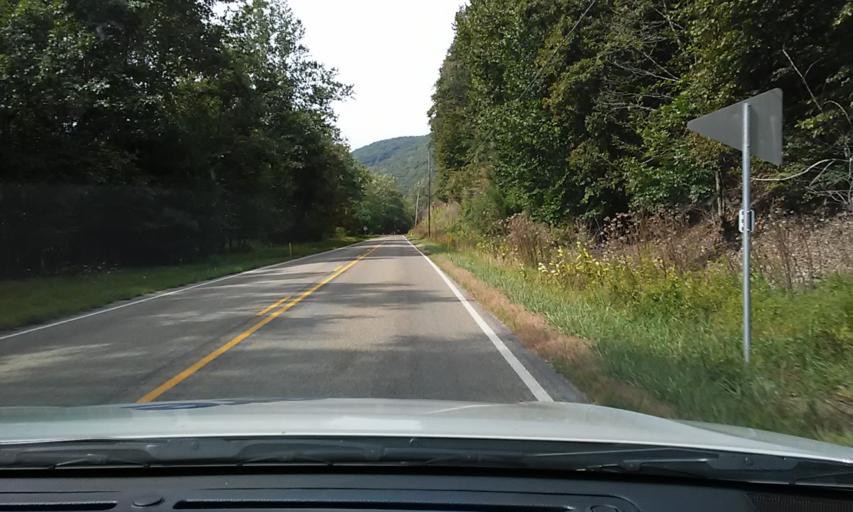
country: US
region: Pennsylvania
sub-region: Cameron County
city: Emporium
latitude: 41.3578
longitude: -78.2558
